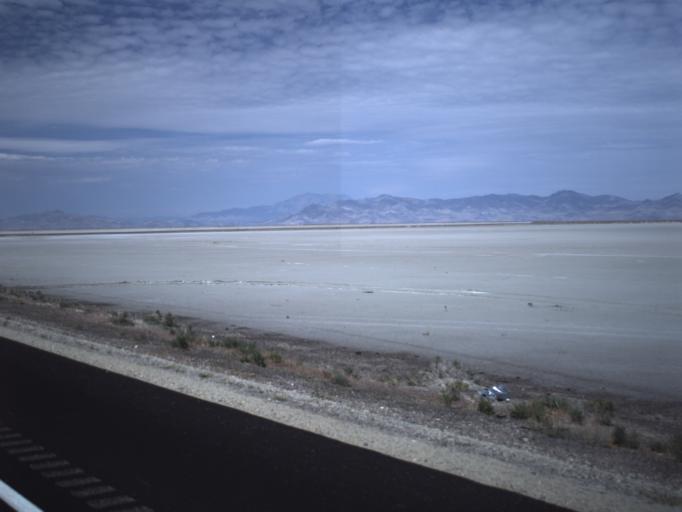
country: US
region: Utah
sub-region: Tooele County
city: Wendover
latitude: 40.7334
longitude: -113.5698
